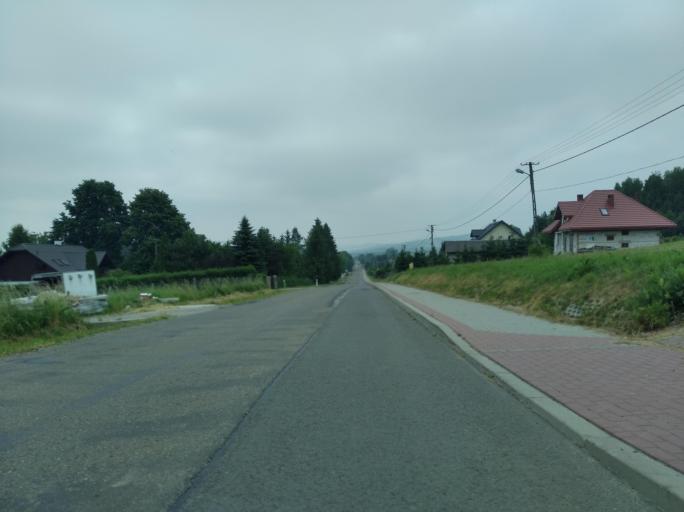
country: PL
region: Subcarpathian Voivodeship
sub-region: Powiat krosnienski
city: Sieniawa
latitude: 49.5776
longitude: 21.9236
